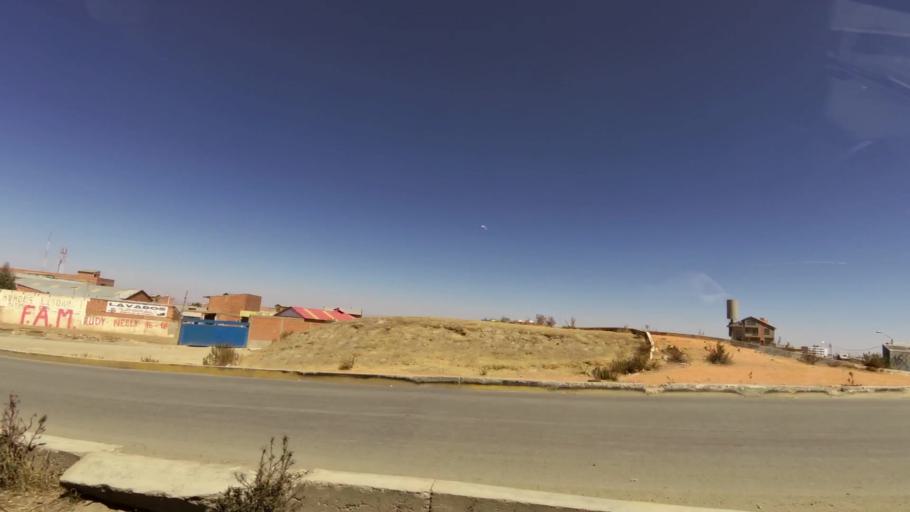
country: BO
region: La Paz
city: La Paz
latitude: -16.5191
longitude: -68.2223
